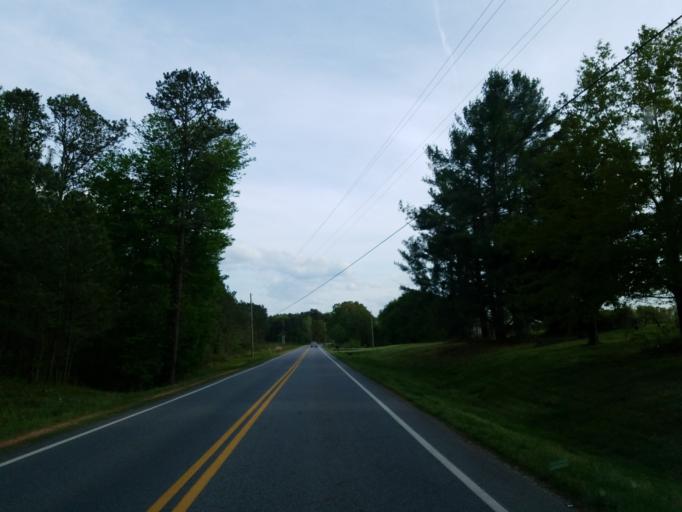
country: US
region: Georgia
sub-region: Cherokee County
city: Ball Ground
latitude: 34.3364
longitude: -84.2649
